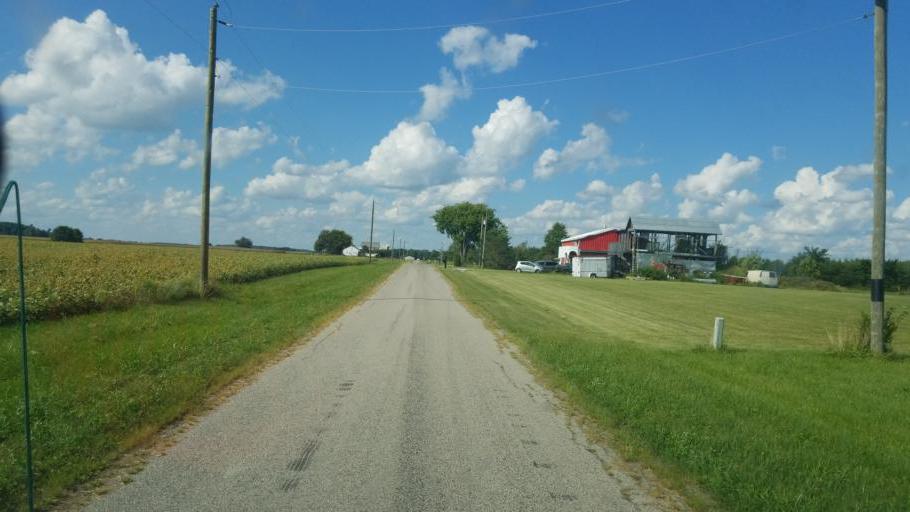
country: US
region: Ohio
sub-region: Union County
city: Richwood
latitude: 40.5014
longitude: -83.3681
